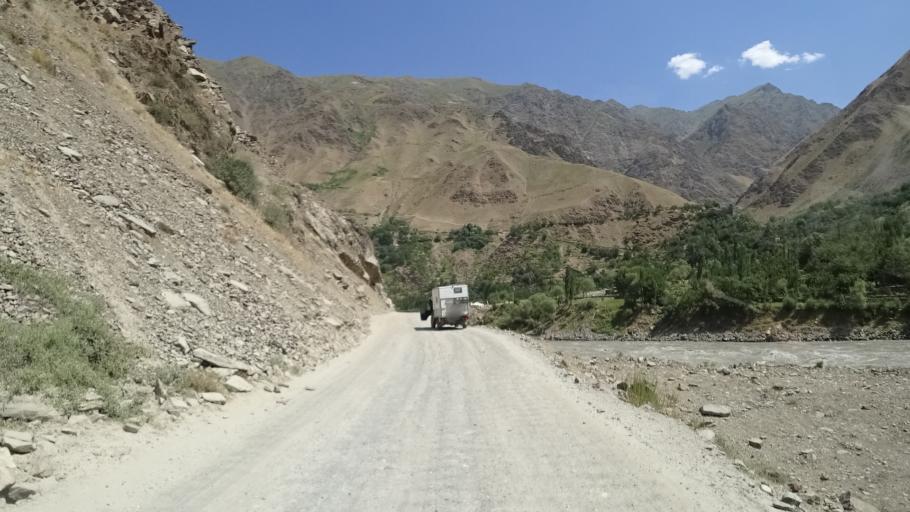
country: AF
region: Badakhshan
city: Maymay
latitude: 38.4391
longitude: 70.9488
